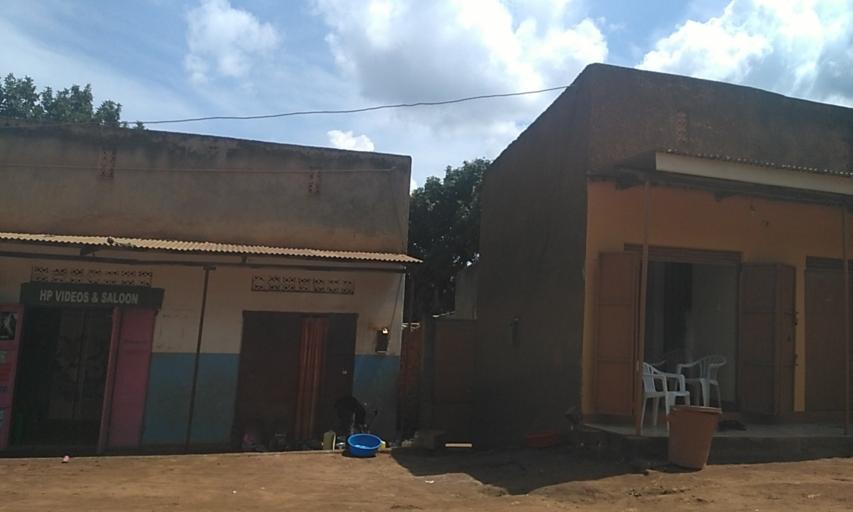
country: UG
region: Central Region
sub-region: Wakiso District
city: Wakiso
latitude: 0.3925
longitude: 32.4644
